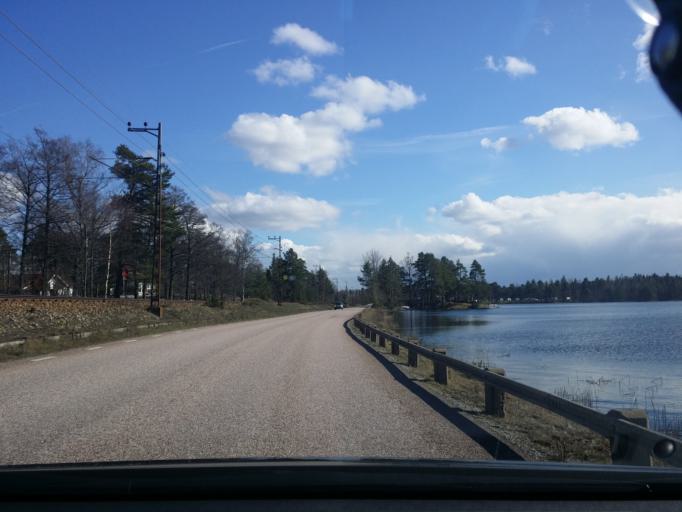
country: SE
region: Vaestmanland
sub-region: Sala Kommun
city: Sala
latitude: 59.9619
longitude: 16.5129
